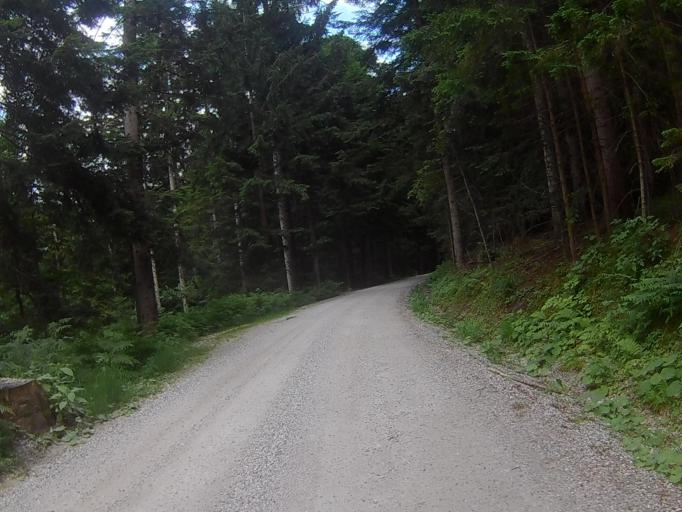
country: SI
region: Ruse
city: Ruse
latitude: 46.5192
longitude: 15.5106
